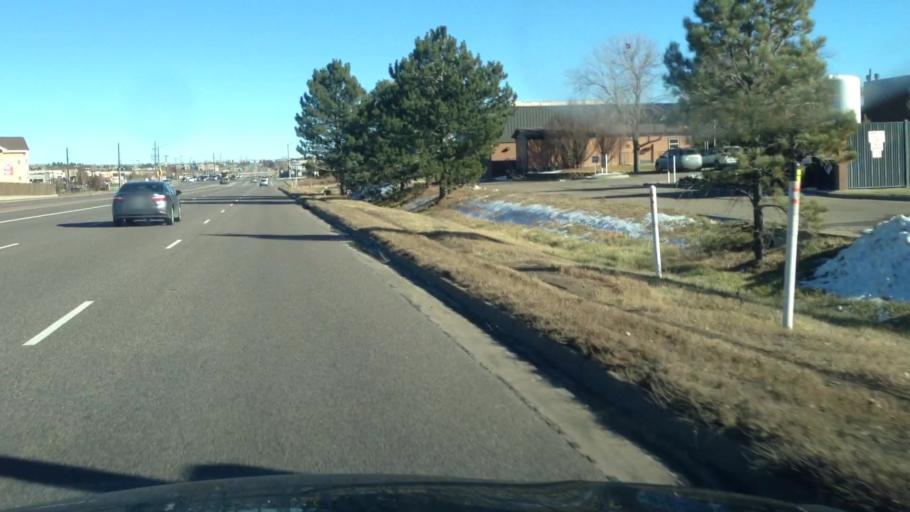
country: US
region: Colorado
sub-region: Arapahoe County
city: Dove Valley
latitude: 39.5948
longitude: -104.8250
